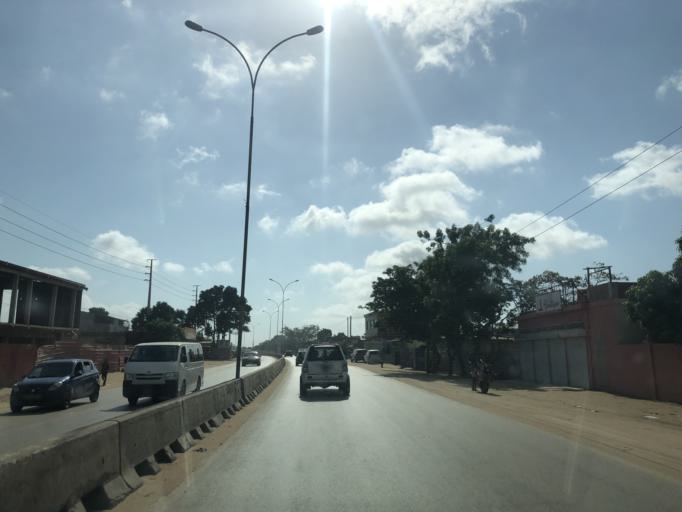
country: AO
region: Luanda
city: Luanda
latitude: -8.9016
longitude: 13.2519
